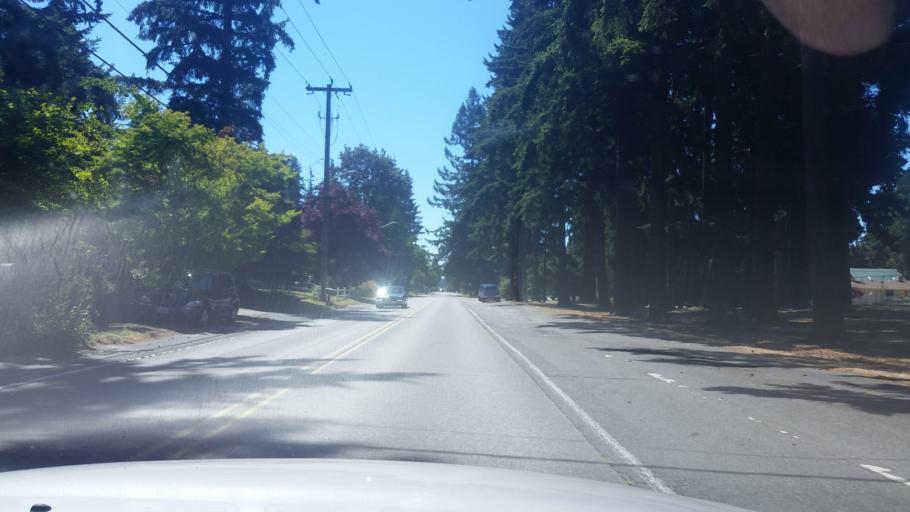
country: US
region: Washington
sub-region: King County
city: Shoreline
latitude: 47.7680
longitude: -122.3513
